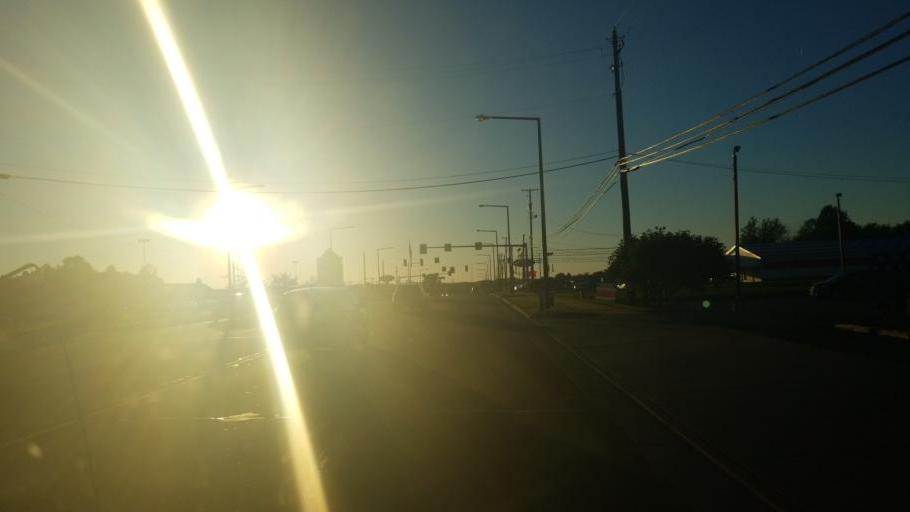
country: US
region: Ohio
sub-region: Stark County
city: Alliance
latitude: 40.9020
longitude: -81.1491
